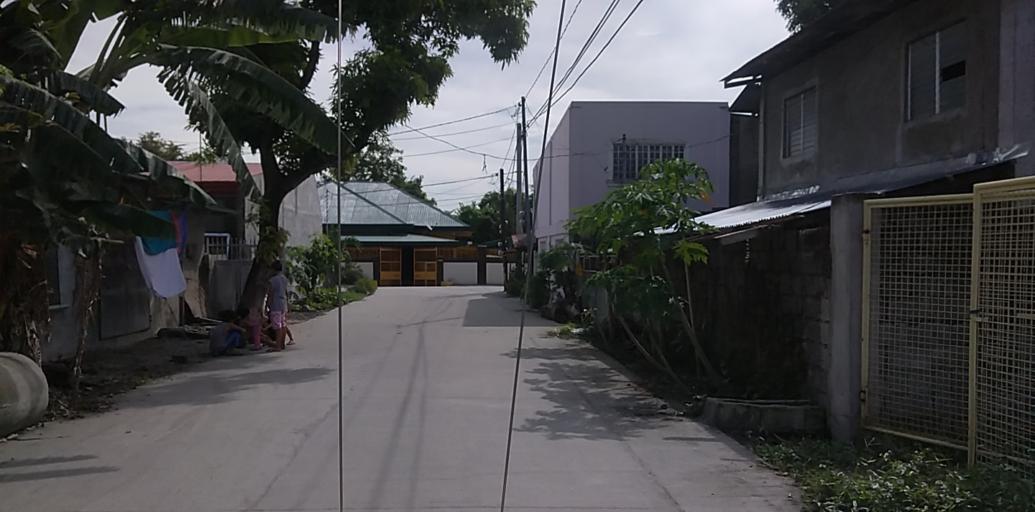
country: PH
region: Central Luzon
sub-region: Province of Pampanga
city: Angeles City
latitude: 15.1283
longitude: 120.5638
